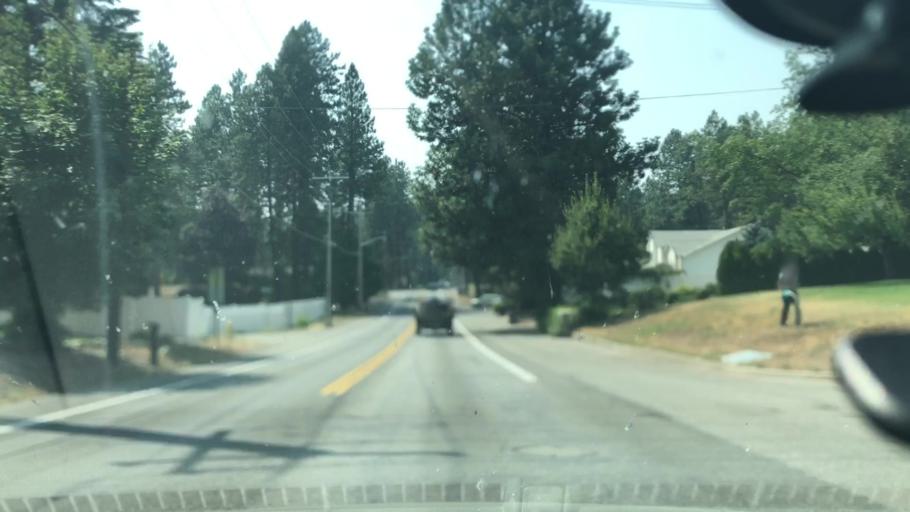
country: US
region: Washington
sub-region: Spokane County
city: Millwood
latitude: 47.6971
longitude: -117.2964
